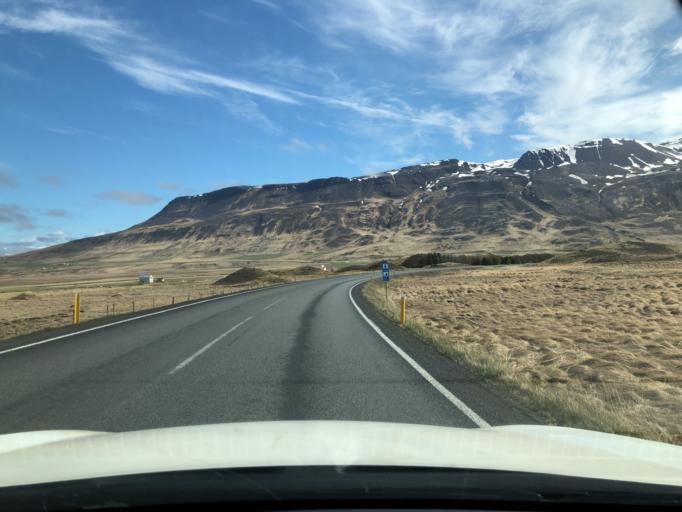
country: IS
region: Northwest
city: Saudarkrokur
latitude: 65.5041
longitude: -20.3879
